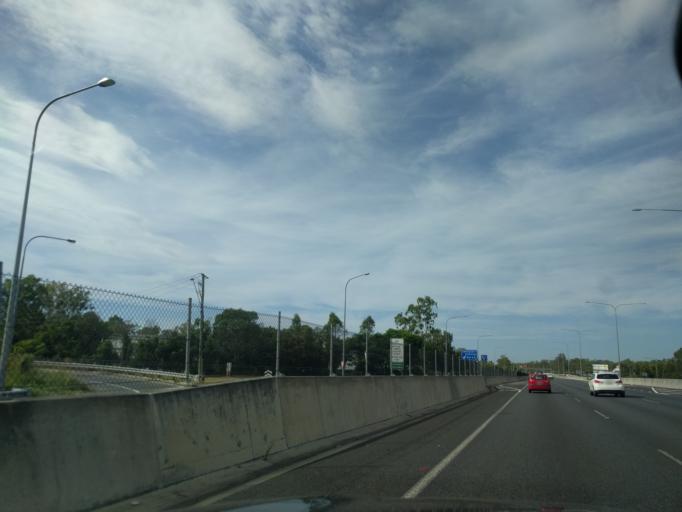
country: AU
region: Queensland
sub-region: Brisbane
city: Wacol
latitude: -27.5890
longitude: 152.9268
